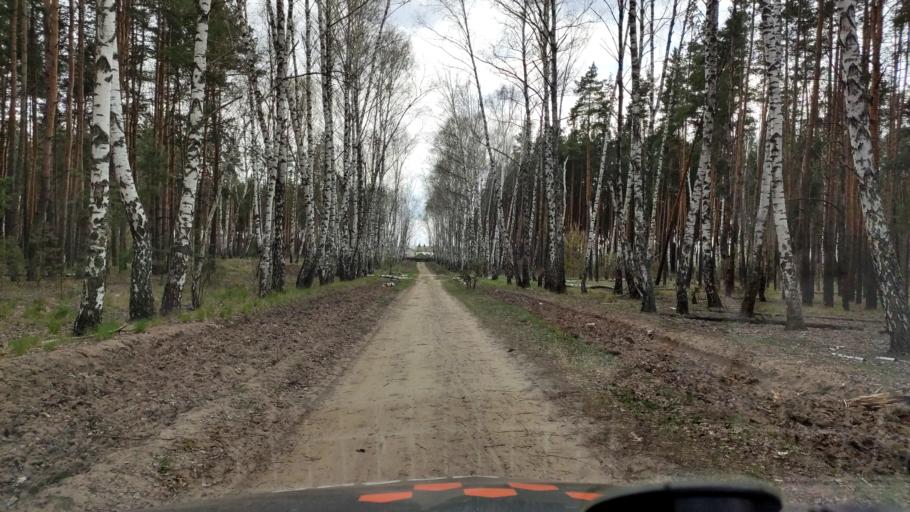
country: RU
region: Voronezj
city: Somovo
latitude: 51.7453
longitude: 39.2755
